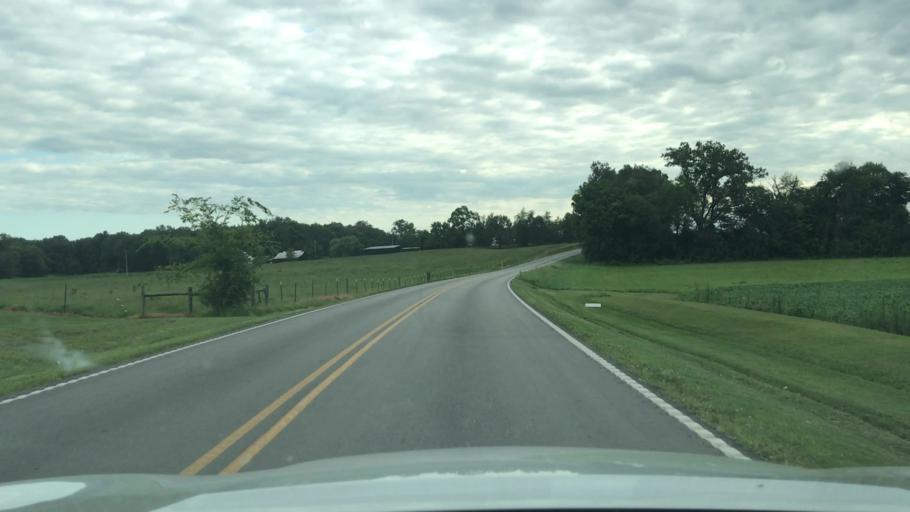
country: US
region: Kentucky
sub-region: Todd County
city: Elkton
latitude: 36.7342
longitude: -87.1884
